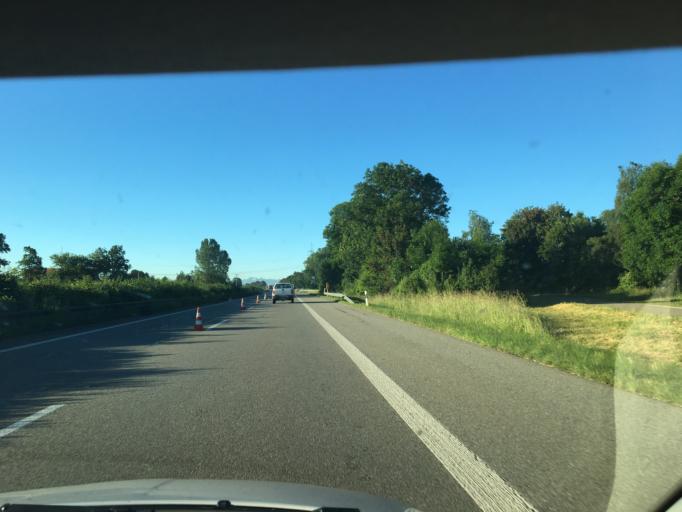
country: DE
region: Bavaria
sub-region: Swabia
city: Woringen
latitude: 47.9429
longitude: 10.1983
